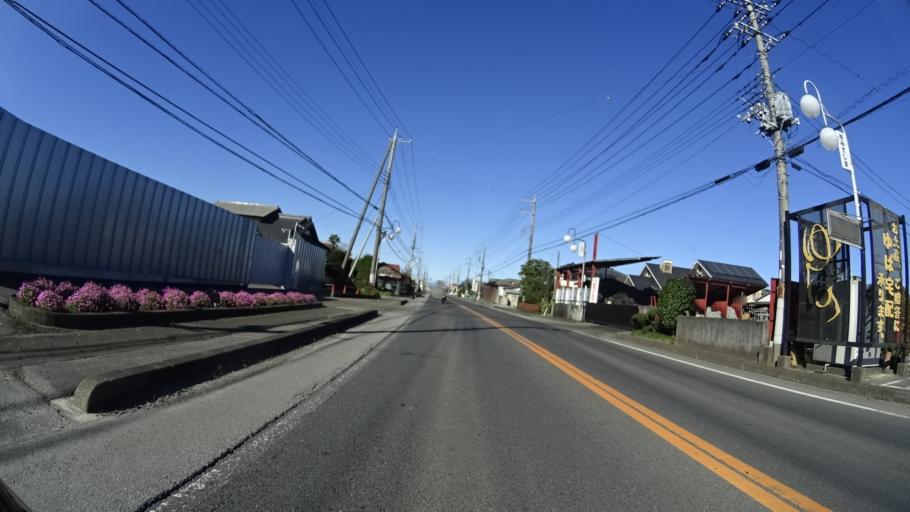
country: JP
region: Tochigi
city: Kanuma
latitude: 36.5167
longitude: 139.7519
